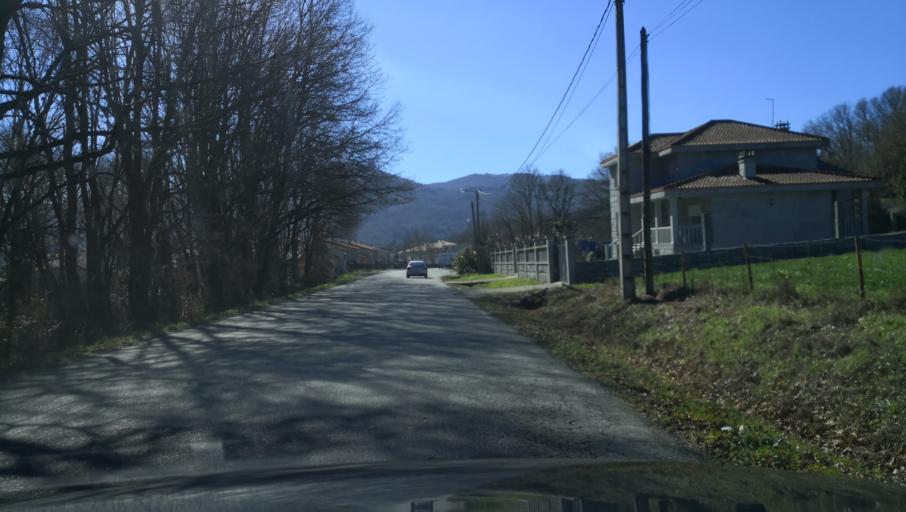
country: ES
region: Galicia
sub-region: Provincia de Ourense
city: Allariz
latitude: 42.1977
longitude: -7.8068
